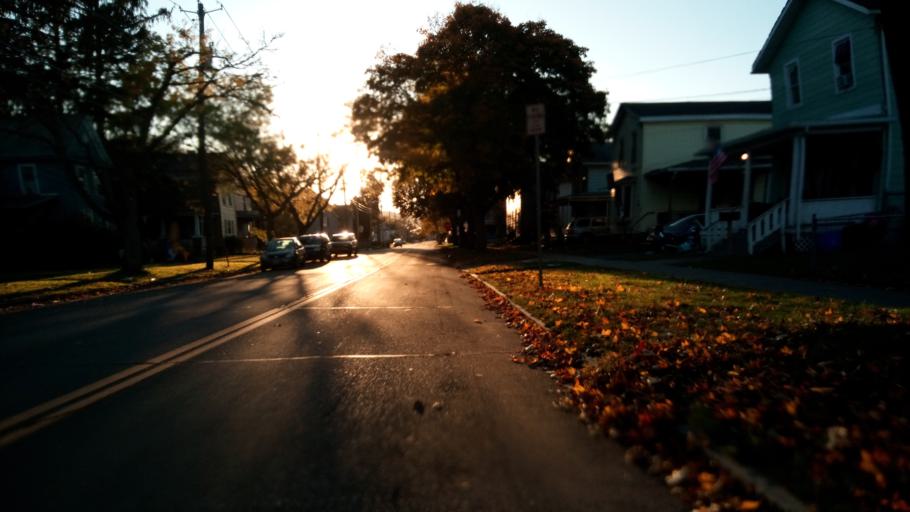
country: US
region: New York
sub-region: Chemung County
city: Elmira
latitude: 42.0830
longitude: -76.8078
